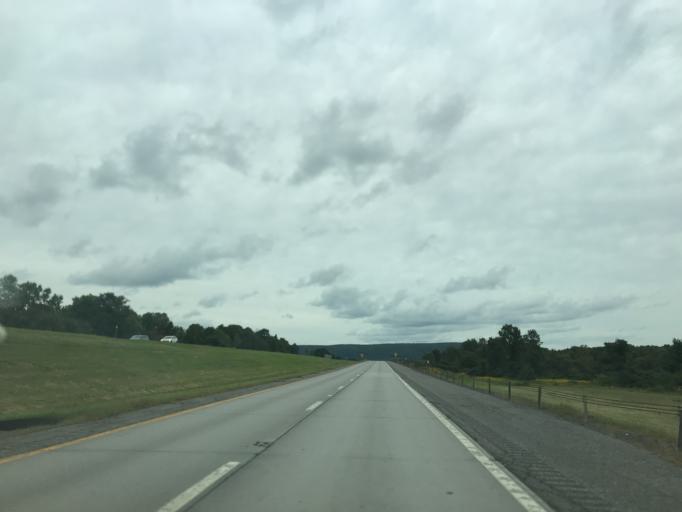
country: US
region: New York
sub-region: Otsego County
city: Oneonta
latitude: 42.4707
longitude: -74.9991
